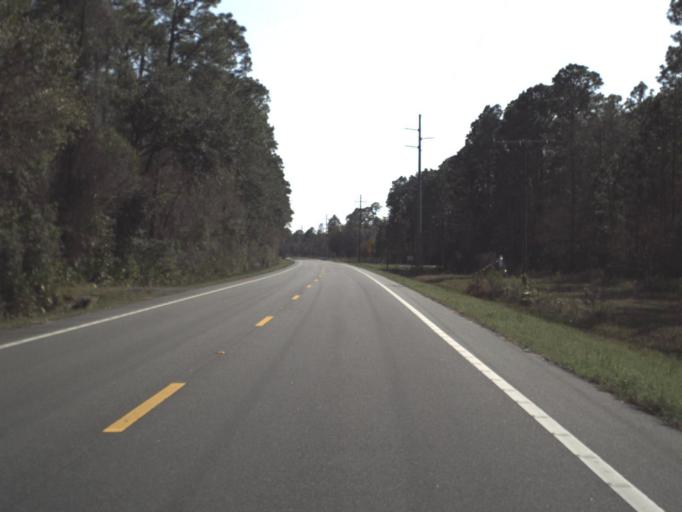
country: US
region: Florida
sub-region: Wakulla County
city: Crawfordville
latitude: 30.0040
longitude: -84.5038
